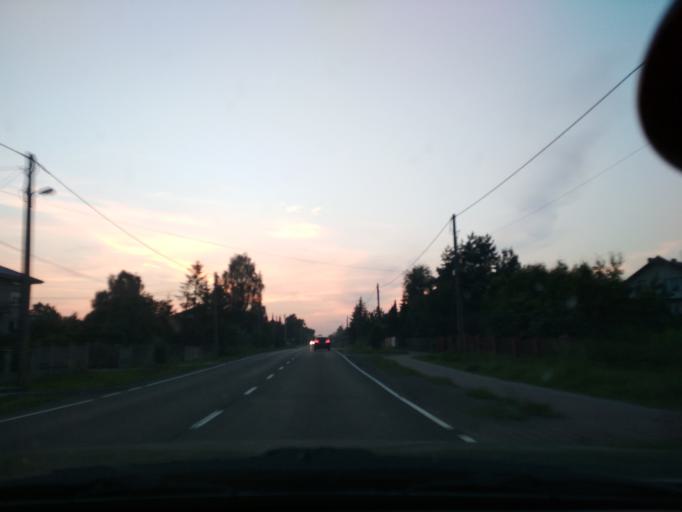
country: PL
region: Silesian Voivodeship
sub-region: Powiat zawiercianski
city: Ogrodzieniec
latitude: 50.4691
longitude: 19.4851
